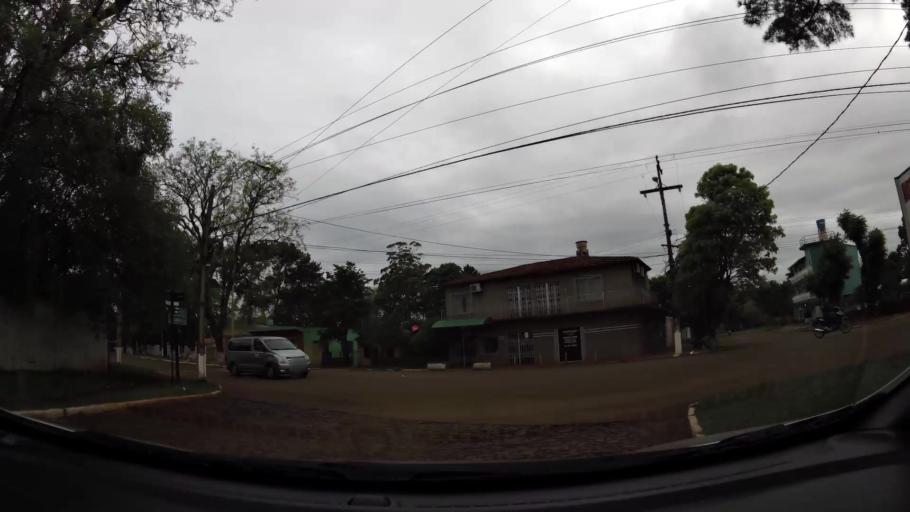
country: PY
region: Alto Parana
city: Ciudad del Este
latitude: -25.4095
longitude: -54.6405
